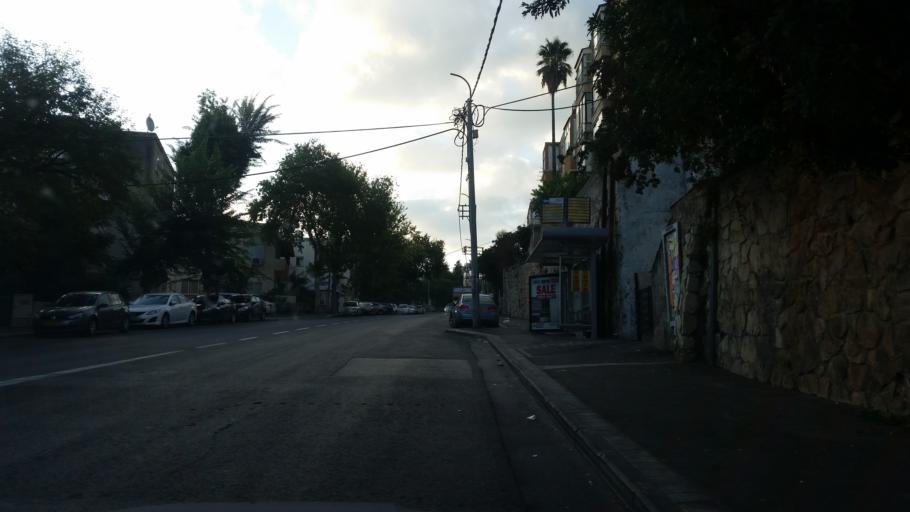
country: IL
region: Haifa
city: Haifa
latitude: 32.8012
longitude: 35.0108
